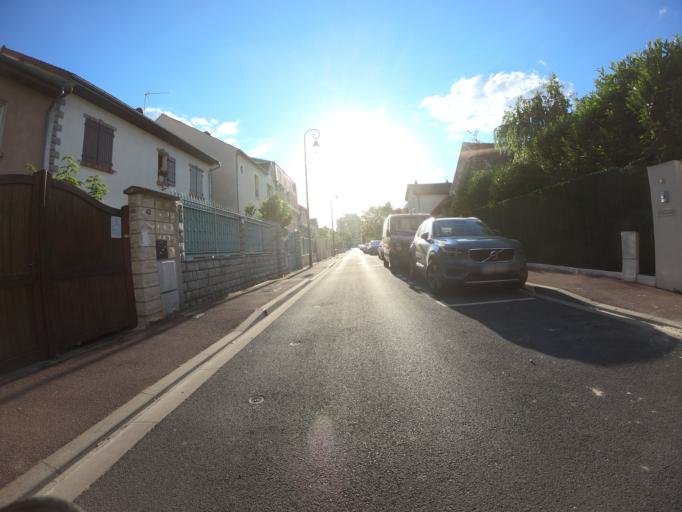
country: FR
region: Ile-de-France
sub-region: Departement du Val-de-Marne
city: Fresnes
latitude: 48.7583
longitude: 2.3112
